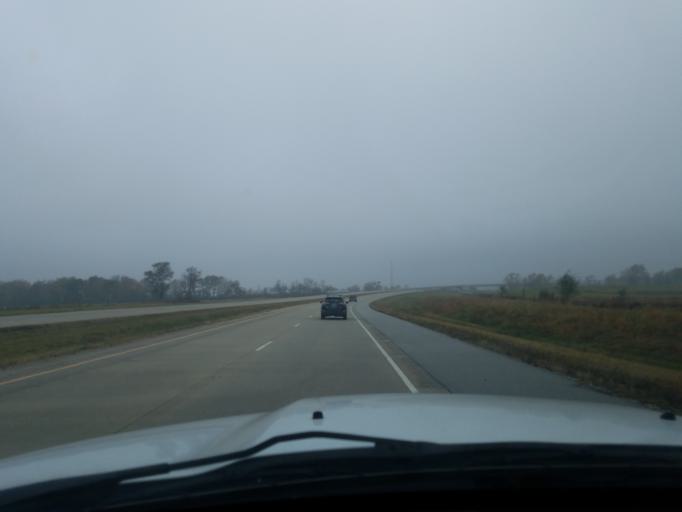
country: US
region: Indiana
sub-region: Howard County
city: Kokomo
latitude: 40.5376
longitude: -86.1192
